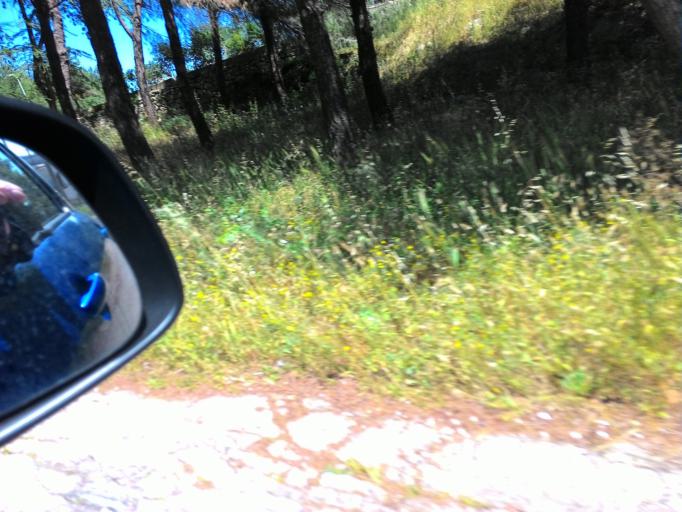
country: IT
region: Apulia
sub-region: Provincia di Bari
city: Putignano
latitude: 40.8359
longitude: 17.1463
